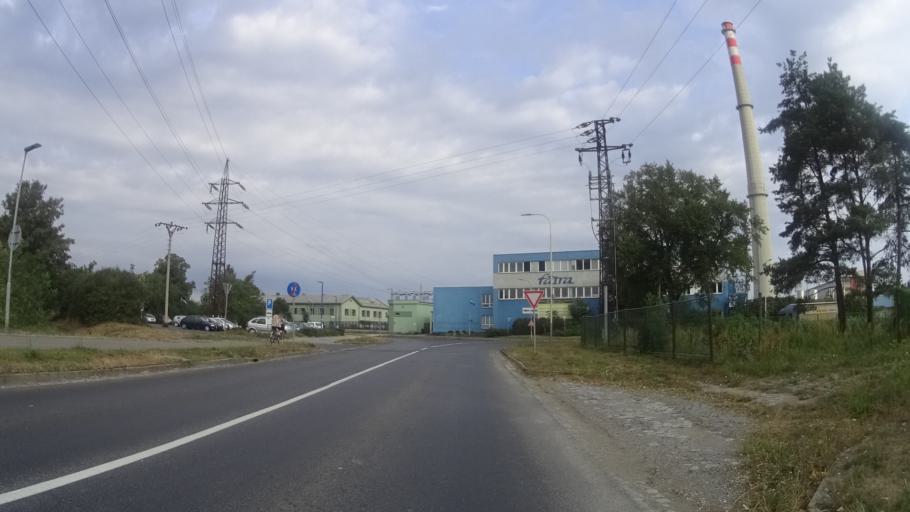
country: CZ
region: Zlin
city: Chropyne
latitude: 49.3570
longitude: 17.3715
